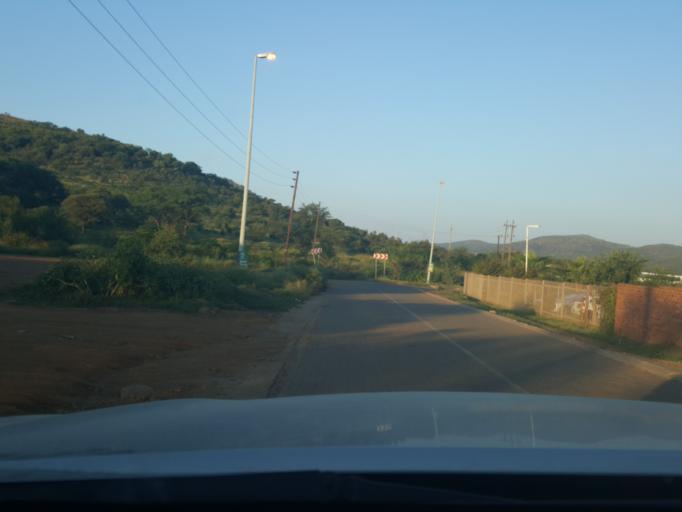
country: ZA
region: North-West
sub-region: Ngaka Modiri Molema District Municipality
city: Zeerust
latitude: -25.5427
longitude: 26.0853
